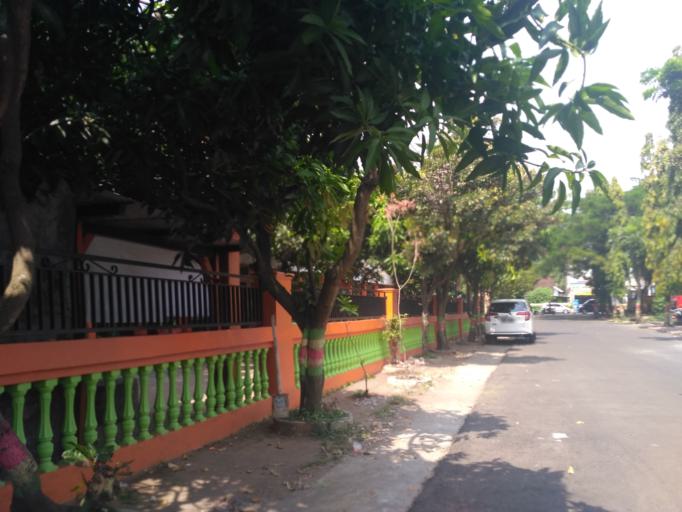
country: ID
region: Central Java
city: Semarang
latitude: -7.0508
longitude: 110.4262
